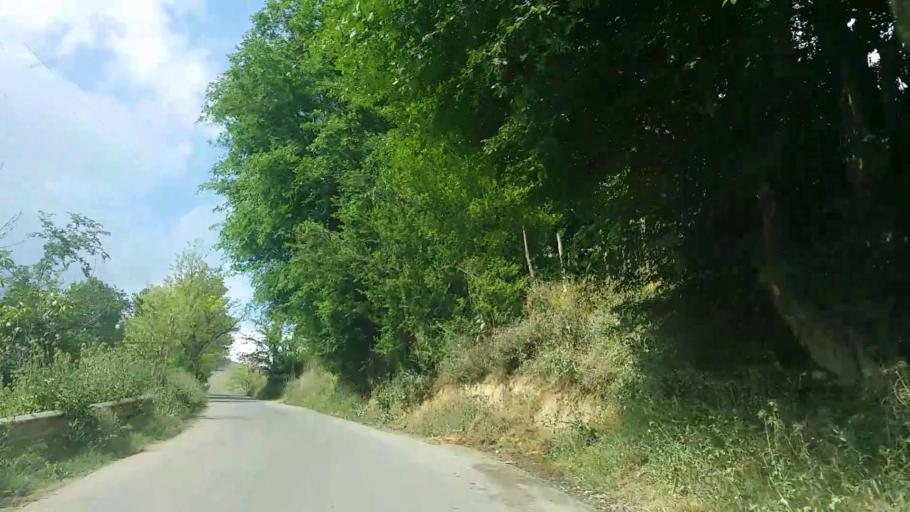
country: IR
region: Mazandaran
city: Chalus
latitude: 36.5193
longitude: 51.2600
